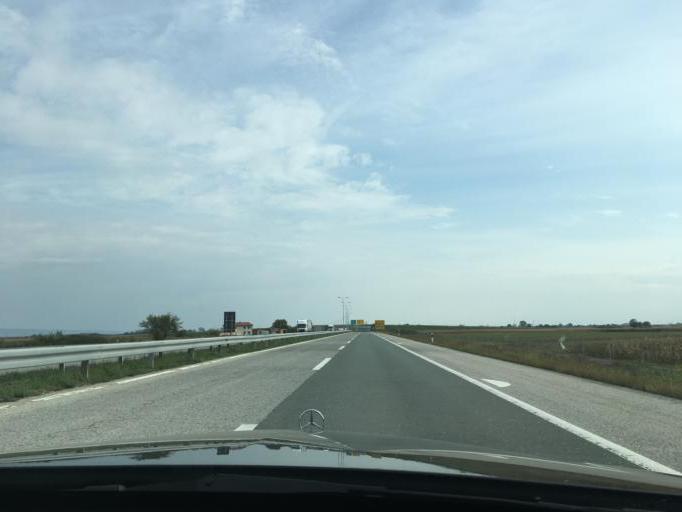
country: RS
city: Ravnje
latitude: 45.0402
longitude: 19.3742
